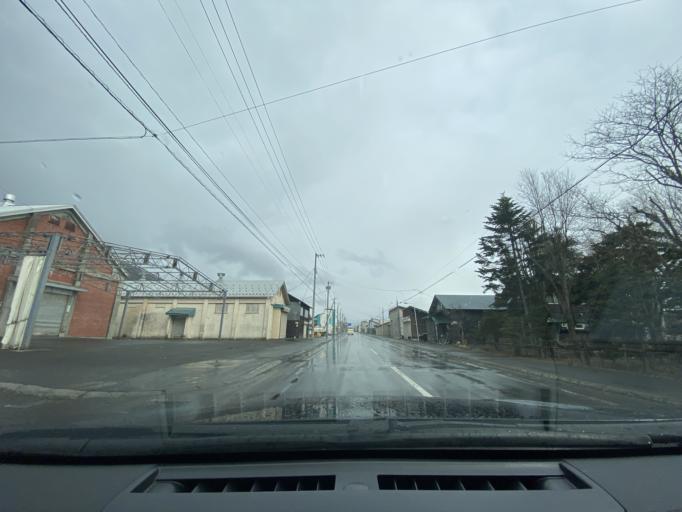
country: JP
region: Hokkaido
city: Nayoro
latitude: 44.1365
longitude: 142.4832
